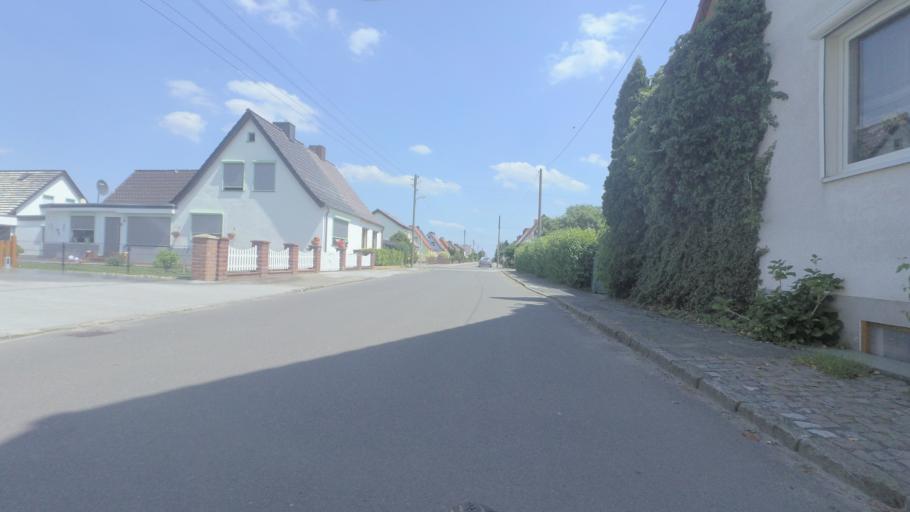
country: DE
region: Saxony-Anhalt
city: Wittenburg
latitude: 51.8450
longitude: 12.6244
